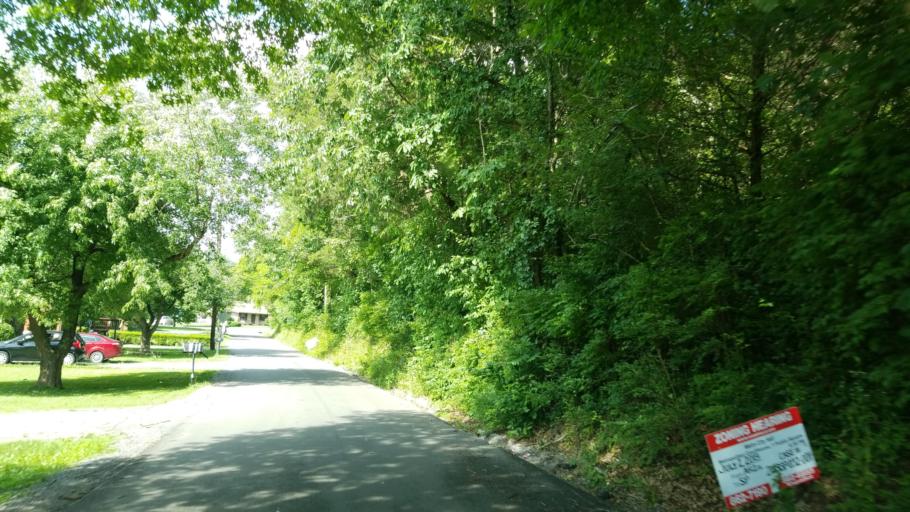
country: US
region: Tennessee
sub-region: Williamson County
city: Brentwood Estates
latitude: 36.0513
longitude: -86.6836
